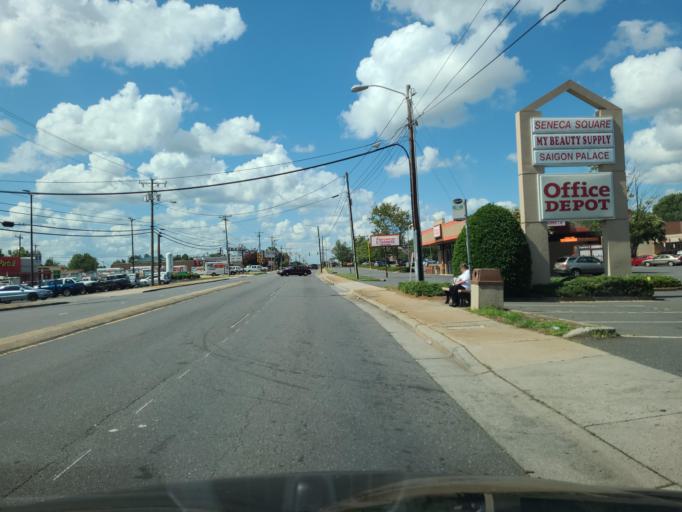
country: US
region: North Carolina
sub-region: Mecklenburg County
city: Charlotte
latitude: 35.1660
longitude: -80.8760
